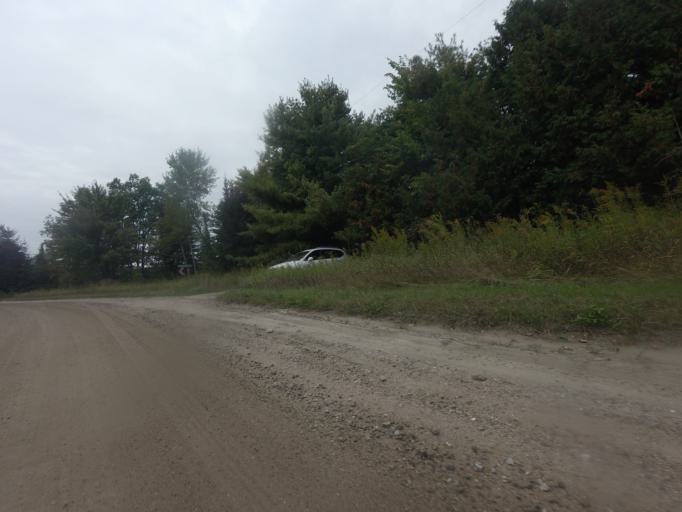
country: CA
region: Quebec
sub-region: Outaouais
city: Maniwaki
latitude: 46.0305
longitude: -75.9454
